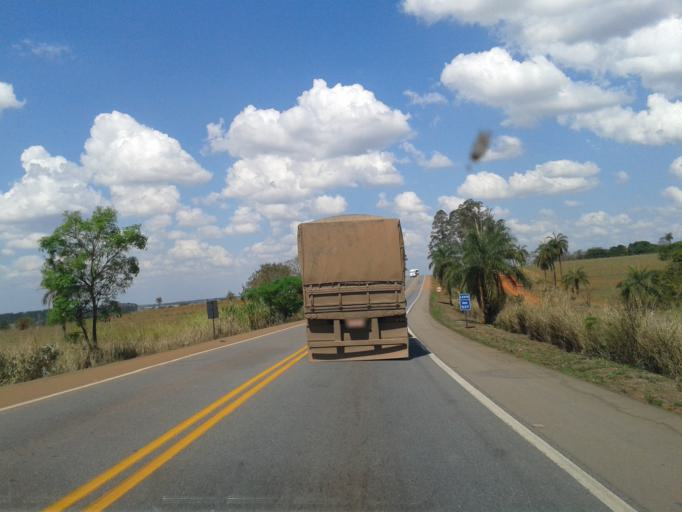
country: BR
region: Minas Gerais
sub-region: Luz
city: Luz
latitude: -19.7580
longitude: -45.8081
